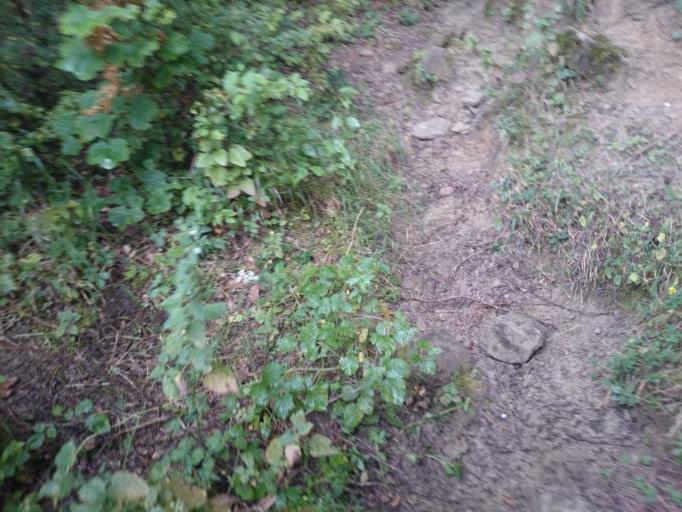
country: AL
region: Elbasan
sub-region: Rrethi i Elbasanit
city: Zavaline
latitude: 40.9514
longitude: 20.2351
